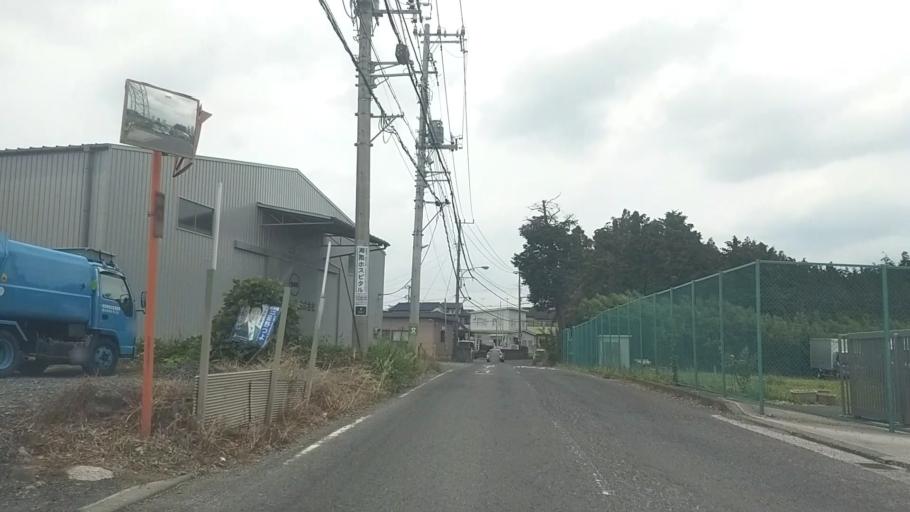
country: JP
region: Kanagawa
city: Fujisawa
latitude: 35.3623
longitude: 139.4351
